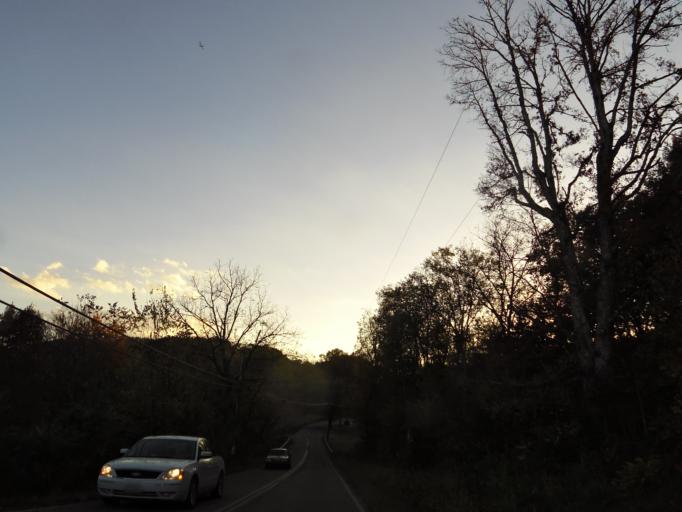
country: US
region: Tennessee
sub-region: Sevier County
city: Seymour
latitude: 35.9344
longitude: -83.7324
